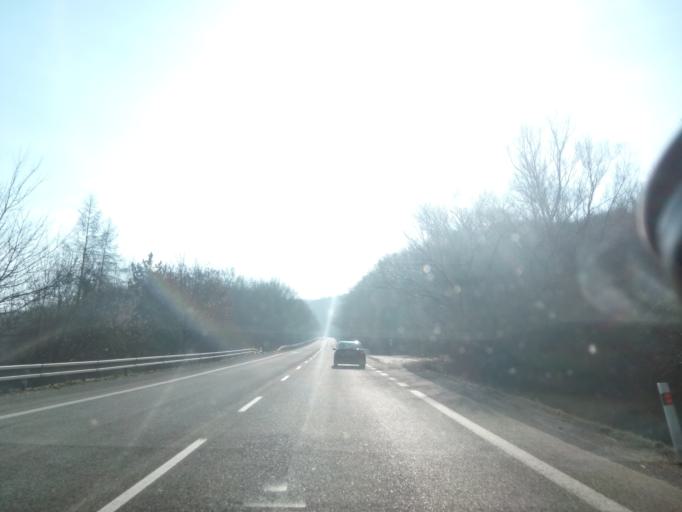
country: SK
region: Kosicky
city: Kosice
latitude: 48.7385
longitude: 21.3665
